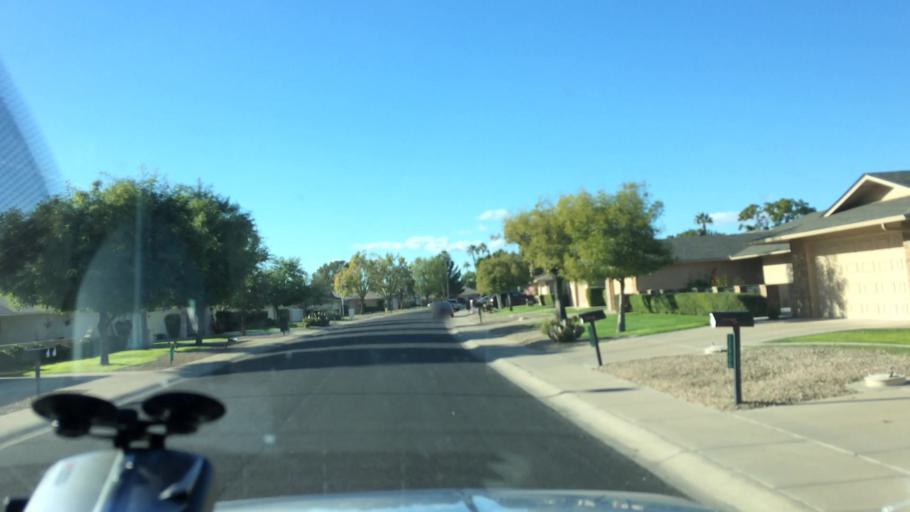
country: US
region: Arizona
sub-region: Maricopa County
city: Sun City West
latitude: 33.6545
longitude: -112.3353
